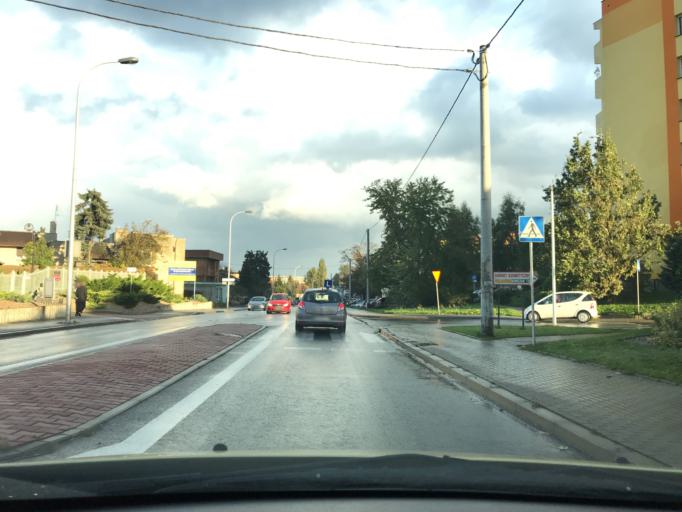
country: PL
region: Greater Poland Voivodeship
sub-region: Kalisz
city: Kalisz
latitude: 51.7625
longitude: 18.0669
